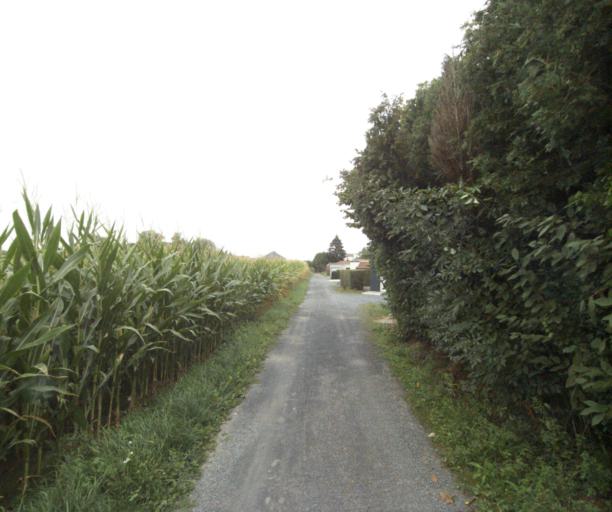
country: FR
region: Nord-Pas-de-Calais
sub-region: Departement du Nord
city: Willems
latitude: 50.6202
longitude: 3.2318
